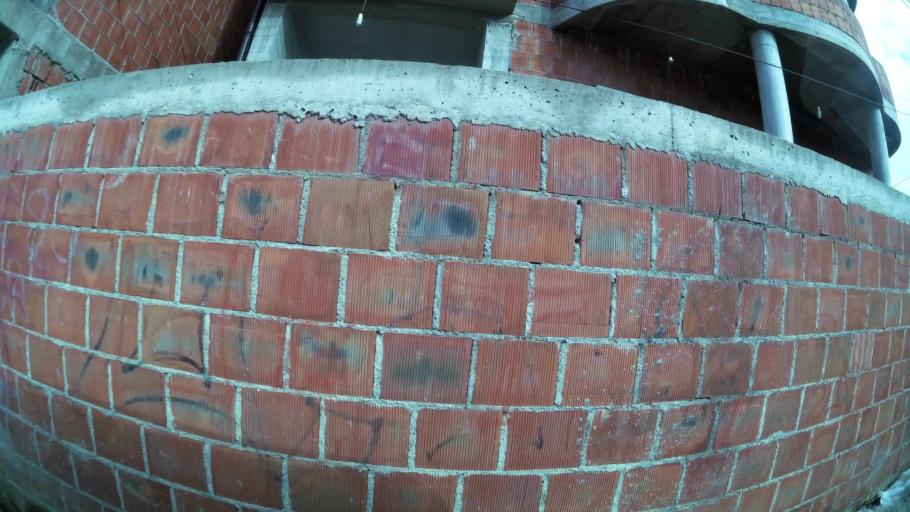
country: XK
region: Pristina
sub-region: Komuna e Prishtines
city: Pristina
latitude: 42.6765
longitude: 21.1559
